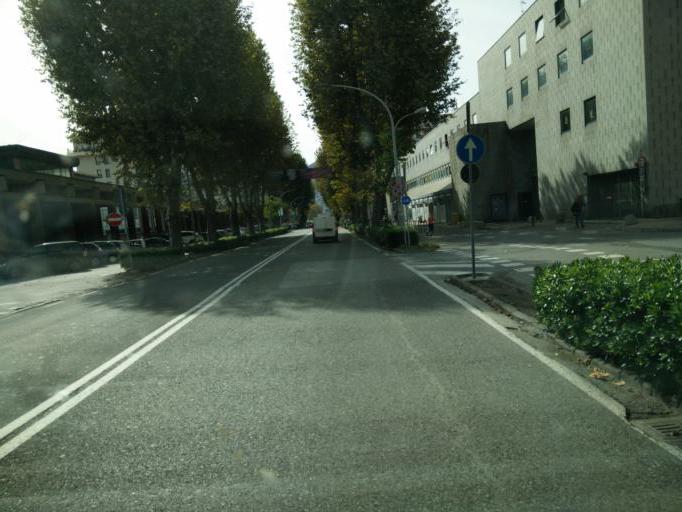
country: IT
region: Liguria
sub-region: Provincia di La Spezia
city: La Spezia
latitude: 44.1127
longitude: 9.8366
